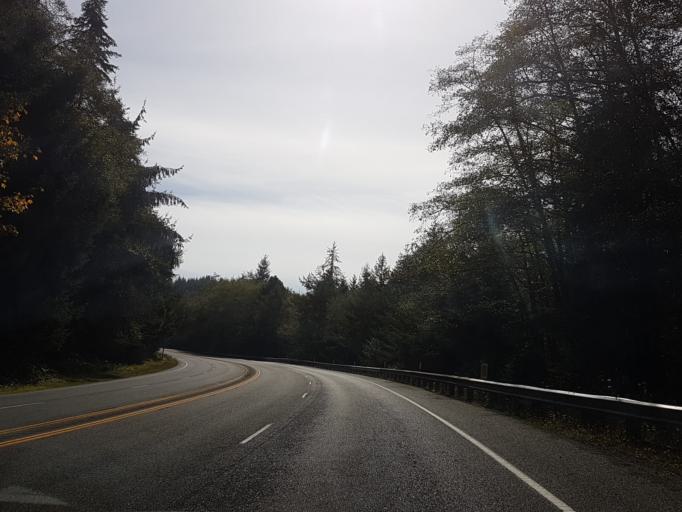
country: US
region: California
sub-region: Del Norte County
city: Bertsch-Oceanview
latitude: 41.4872
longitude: -124.0505
